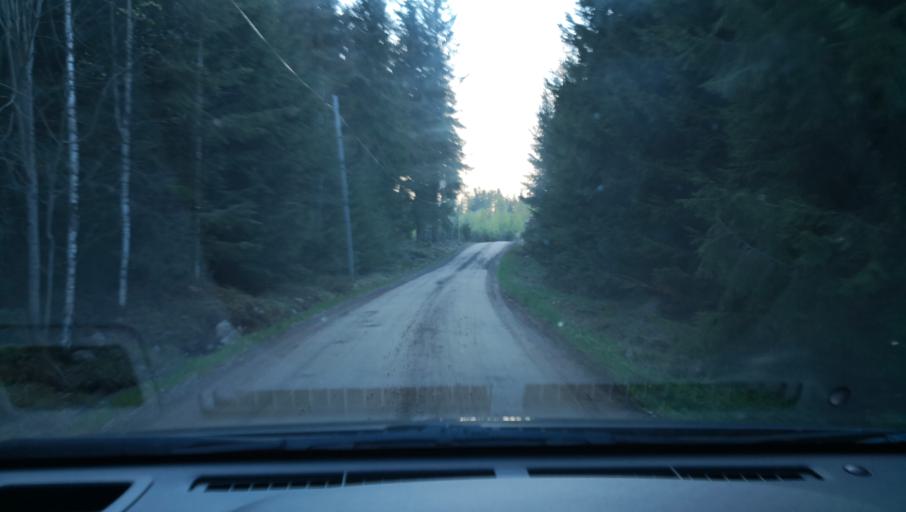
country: SE
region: OErebro
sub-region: Askersunds Kommun
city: Asbro
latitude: 58.9822
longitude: 14.9420
